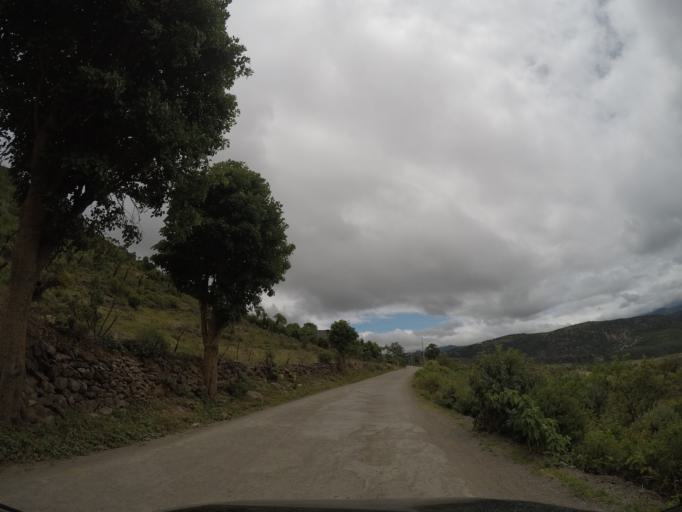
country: MX
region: Oaxaca
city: San Lorenzo Albarradas
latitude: 16.8963
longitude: -96.2614
